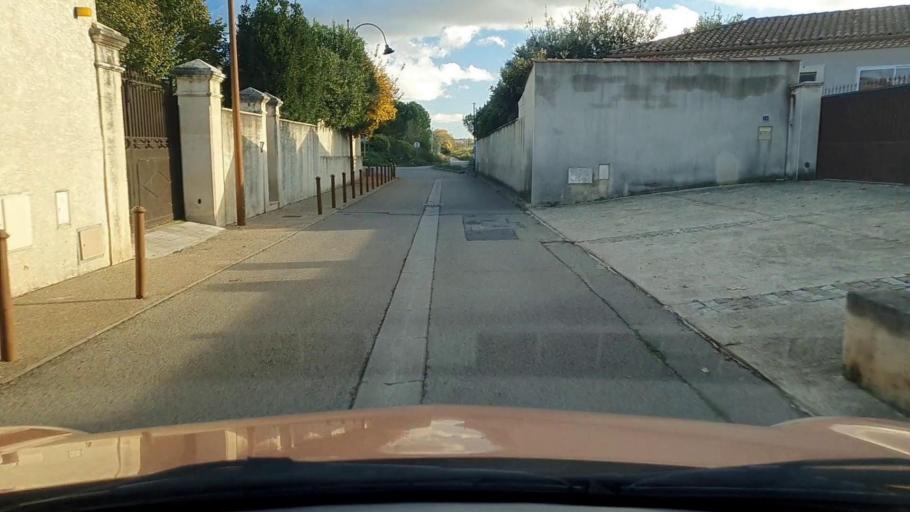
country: FR
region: Languedoc-Roussillon
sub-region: Departement du Gard
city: Bernis
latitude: 43.7650
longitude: 4.2898
